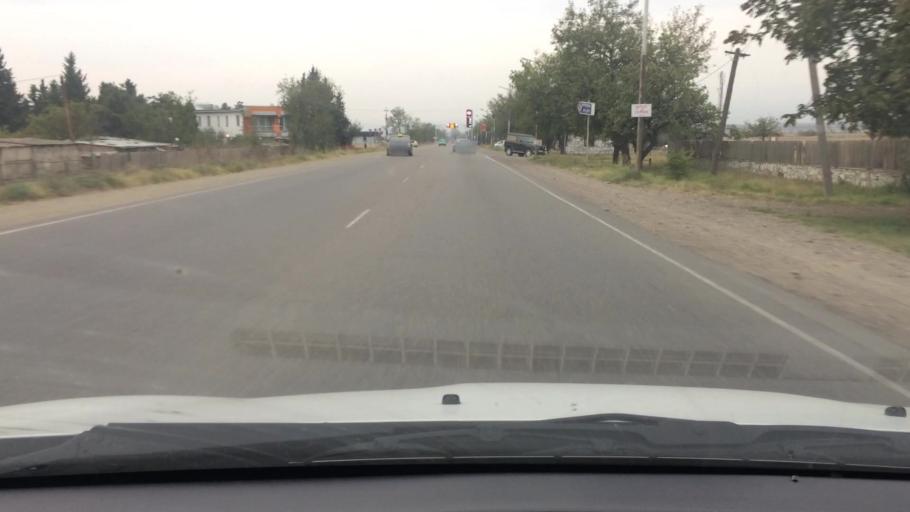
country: GE
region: Kvemo Kartli
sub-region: Marneuli
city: Marneuli
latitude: 41.5762
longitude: 44.7747
